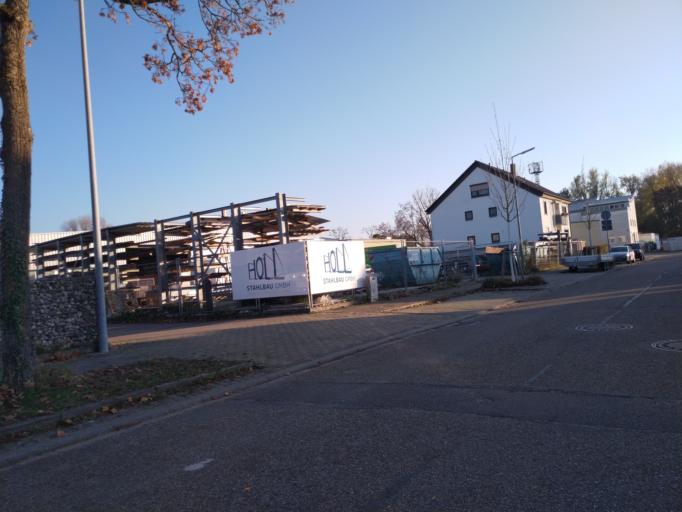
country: DE
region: Baden-Wuerttemberg
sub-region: Karlsruhe Region
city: Rheinstetten
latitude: 49.0058
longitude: 8.3197
